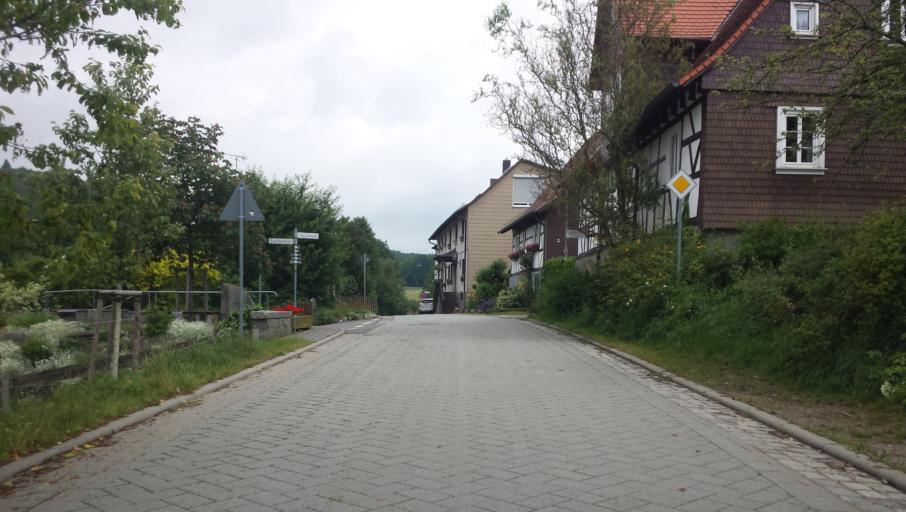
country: DE
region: Hesse
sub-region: Regierungsbezirk Darmstadt
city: Lindenfels
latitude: 49.6897
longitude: 8.7212
